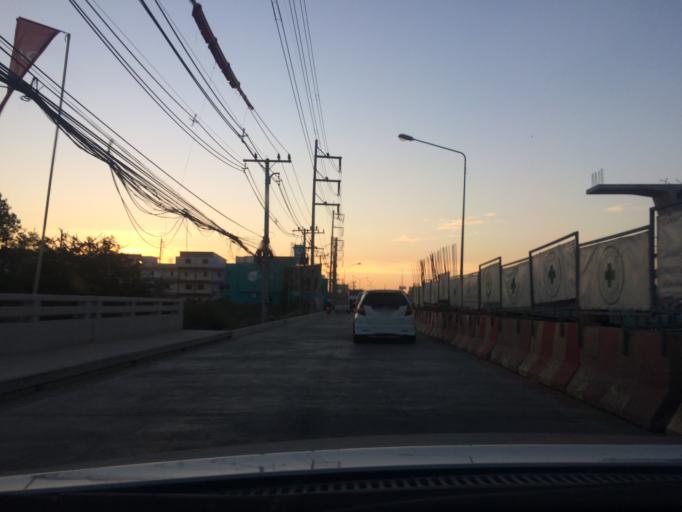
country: TH
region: Phitsanulok
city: Phitsanulok
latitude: 16.8177
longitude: 100.3327
